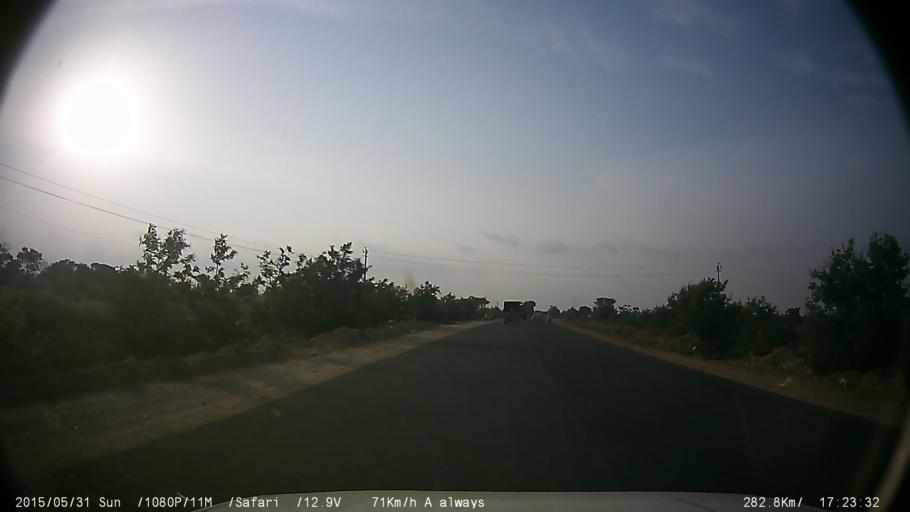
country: IN
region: Karnataka
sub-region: Chamrajnagar
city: Gundlupet
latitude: 11.8408
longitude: 76.6739
